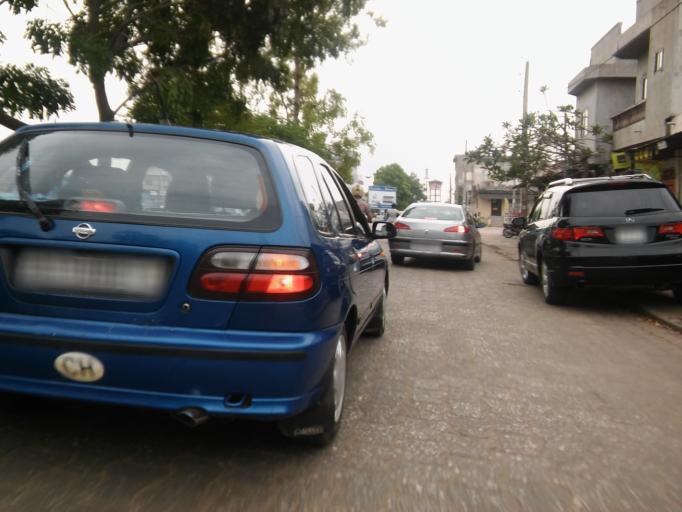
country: BJ
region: Littoral
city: Cotonou
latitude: 6.3882
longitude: 2.3745
